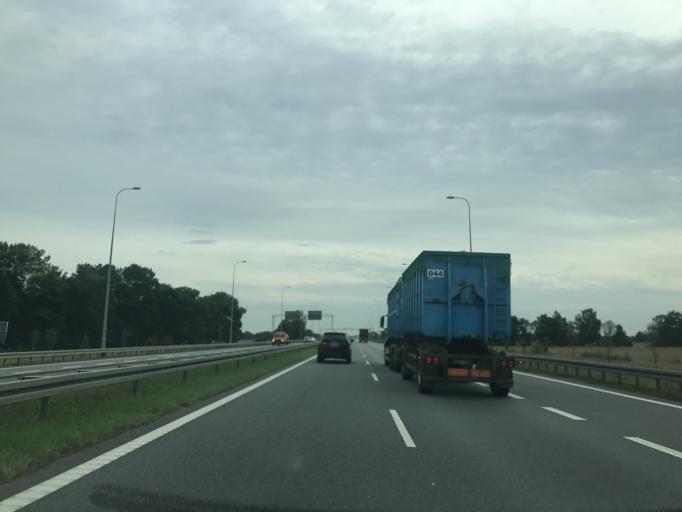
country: PL
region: Pomeranian Voivodeship
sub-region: Powiat gdanski
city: Suchy Dab
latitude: 54.3156
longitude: 18.7528
